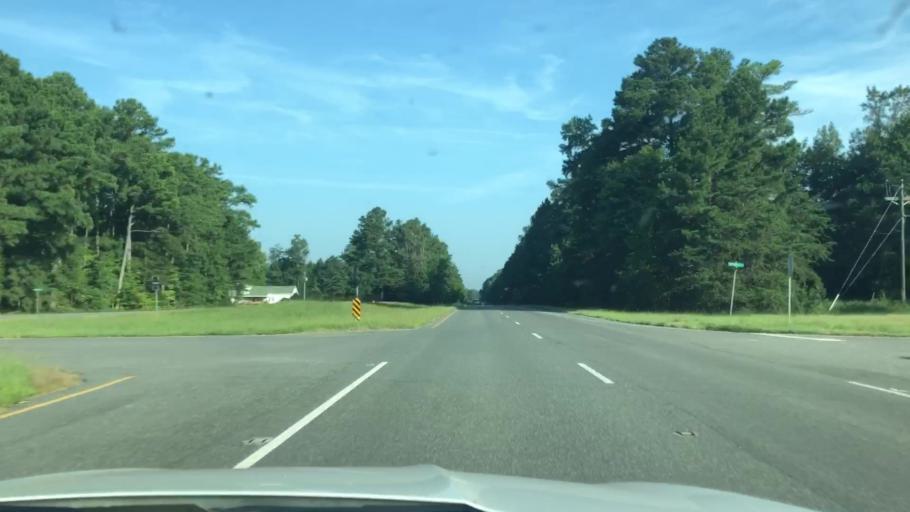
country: US
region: Virginia
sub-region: King and Queen County
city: King and Queen Court House
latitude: 37.7749
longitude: -76.7546
